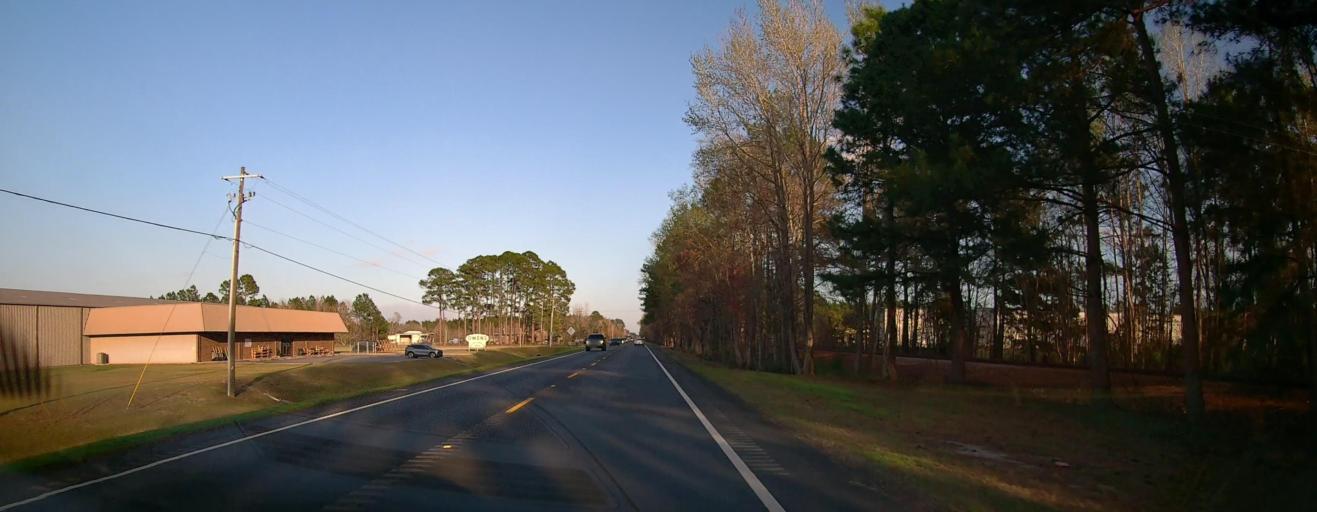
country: US
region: Georgia
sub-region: Bryan County
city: Pembroke
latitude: 32.1349
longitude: -81.6106
